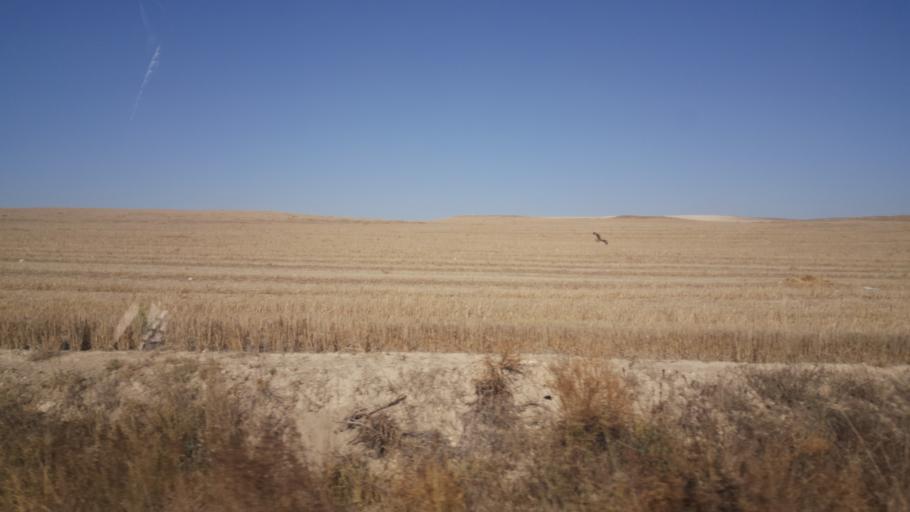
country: TR
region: Konya
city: Celtik
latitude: 39.0912
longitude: 32.0609
